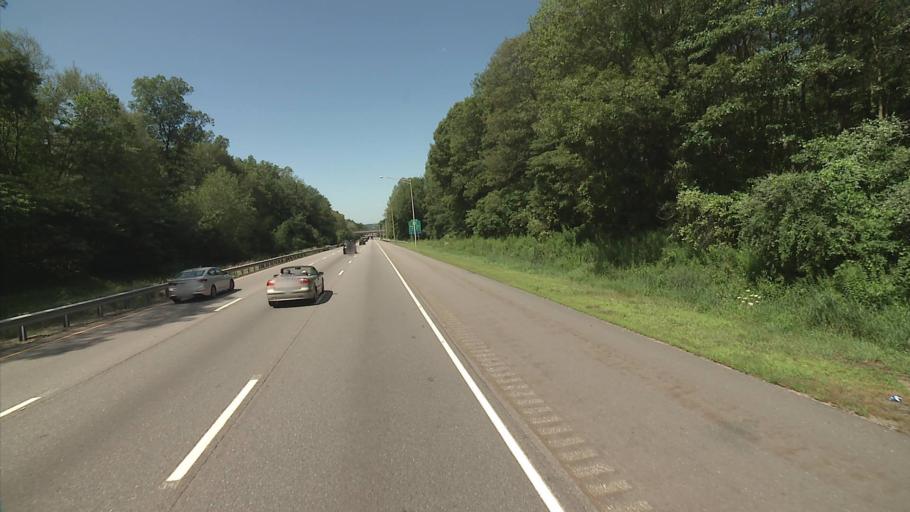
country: US
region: Connecticut
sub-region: New London County
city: Poquonock Bridge
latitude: 41.3698
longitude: -72.0027
